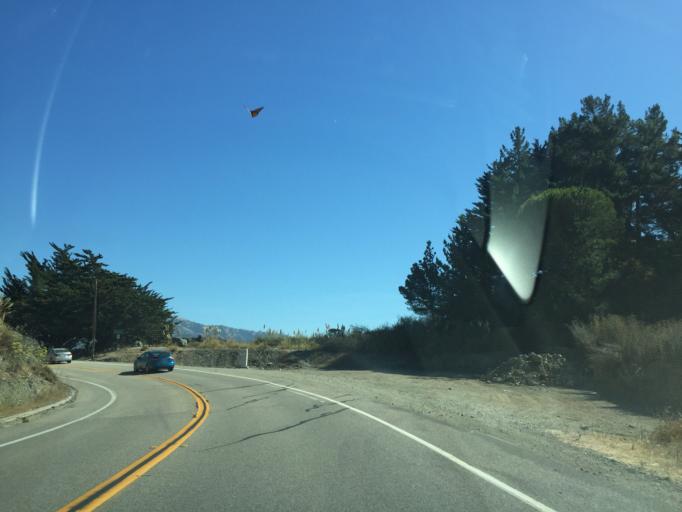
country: US
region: California
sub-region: Monterey County
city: Greenfield
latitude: 36.0208
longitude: -121.5520
